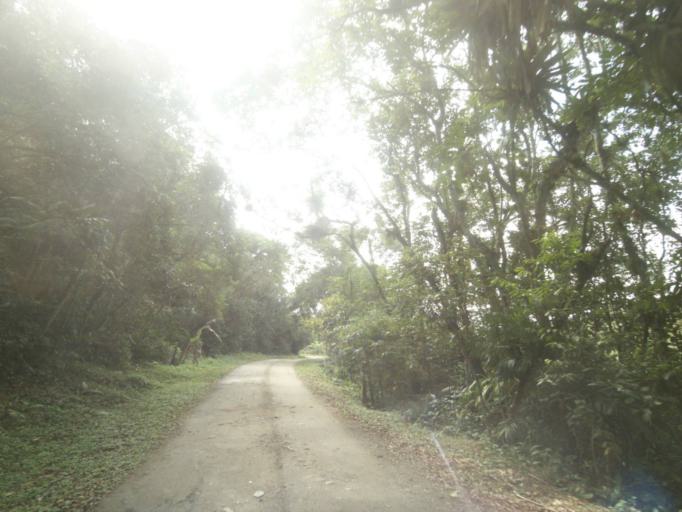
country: BR
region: Parana
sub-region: Paranagua
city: Paranagua
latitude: -25.5580
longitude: -48.6486
